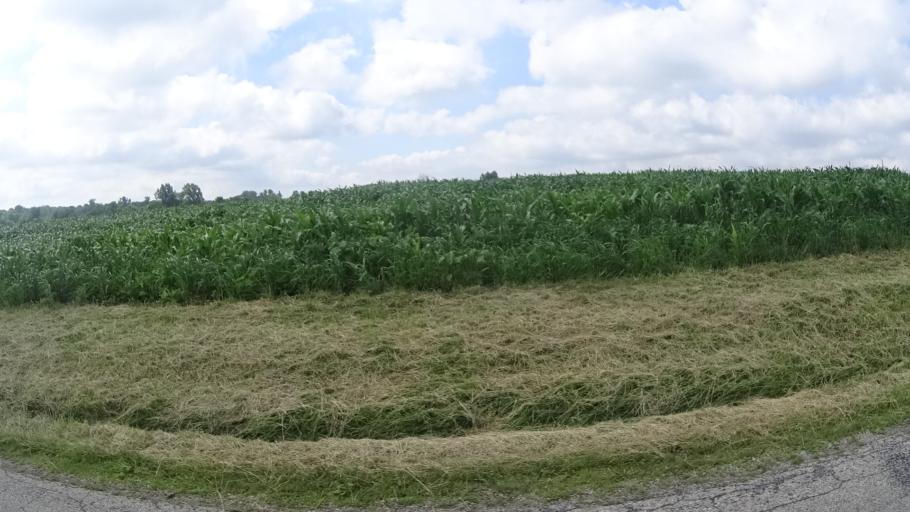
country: US
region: Ohio
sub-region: Huron County
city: Wakeman
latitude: 41.3058
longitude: -82.4120
